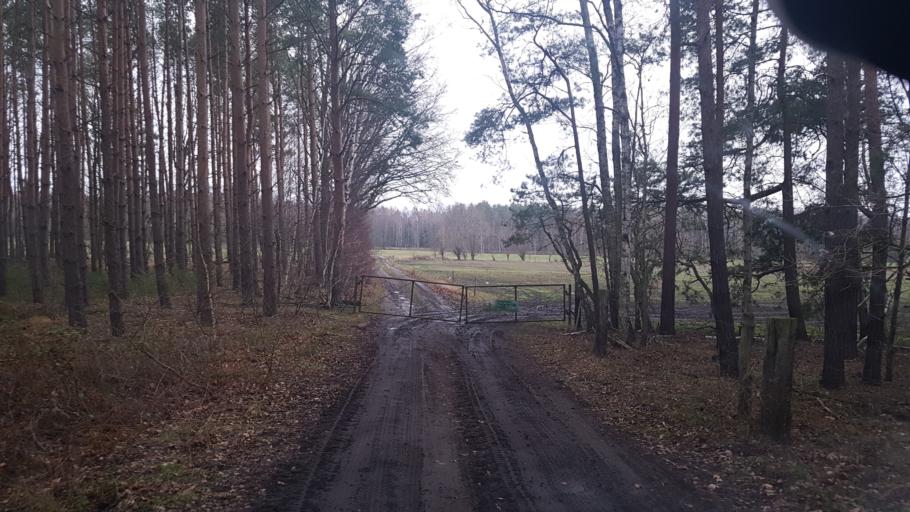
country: DE
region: Brandenburg
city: Ruckersdorf
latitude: 51.5994
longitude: 13.5937
